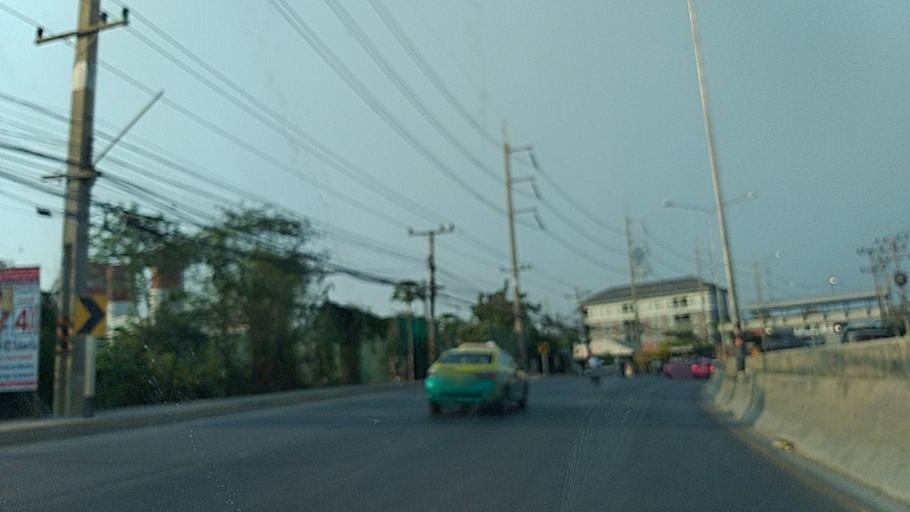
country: TH
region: Phra Nakhon Si Ayutthaya
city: Ban Bang Kadi Pathum Thani
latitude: 13.9929
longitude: 100.5507
